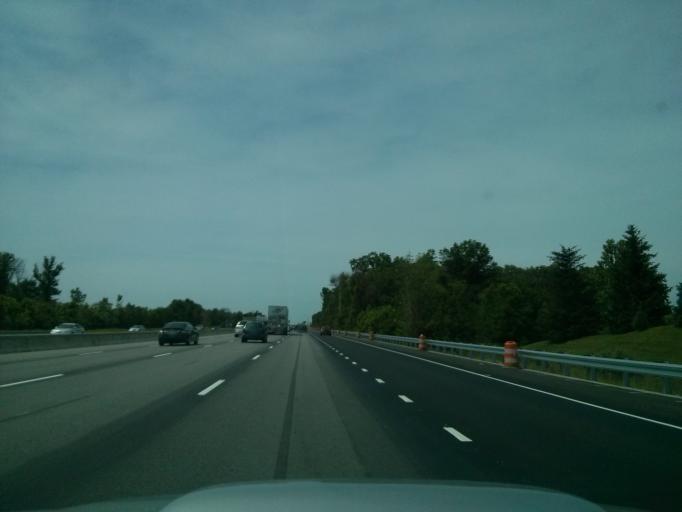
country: US
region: Indiana
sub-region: Hamilton County
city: Fishers
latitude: 39.9411
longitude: -86.0196
